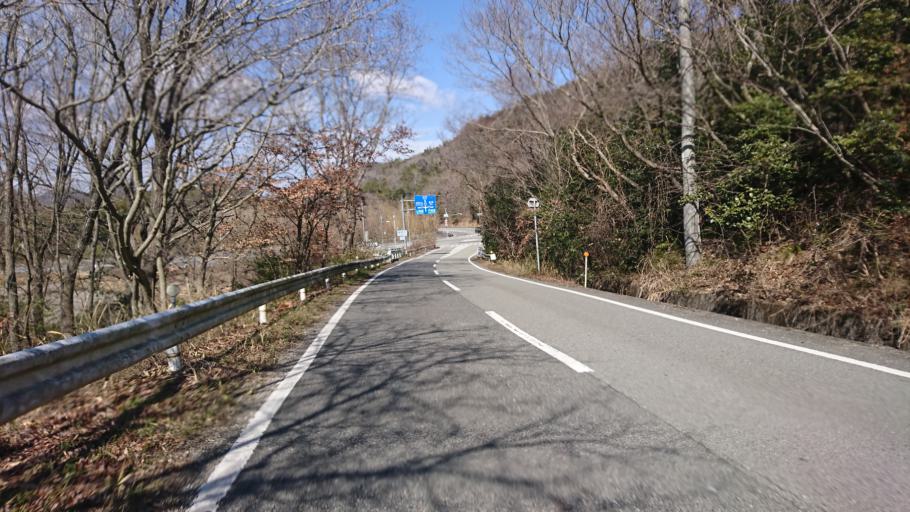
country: JP
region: Hyogo
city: Kakogawacho-honmachi
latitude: 34.8658
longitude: 134.7974
